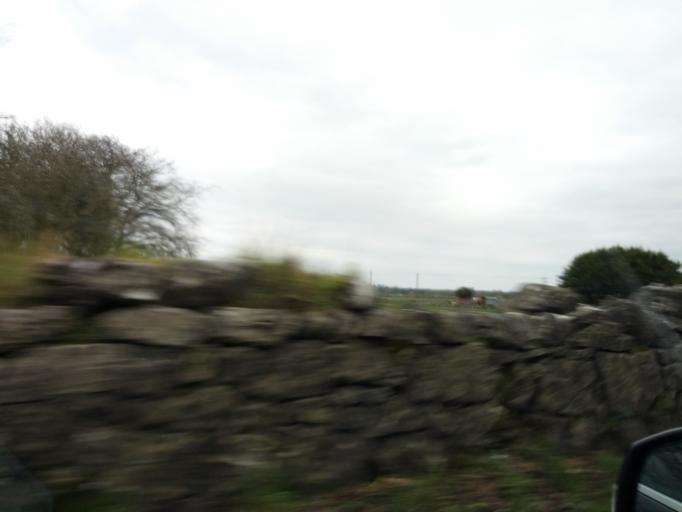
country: IE
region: Connaught
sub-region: County Galway
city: Athenry
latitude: 53.2841
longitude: -8.7439
